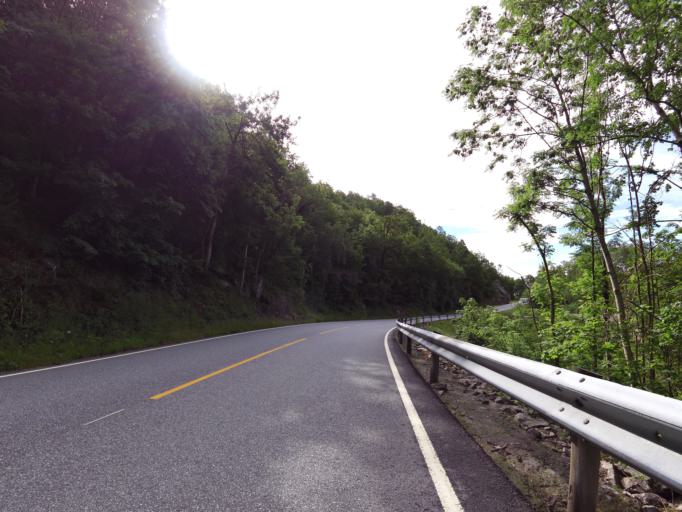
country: NO
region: Vest-Agder
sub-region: Lindesnes
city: Vigeland
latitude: 58.0558
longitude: 7.1814
